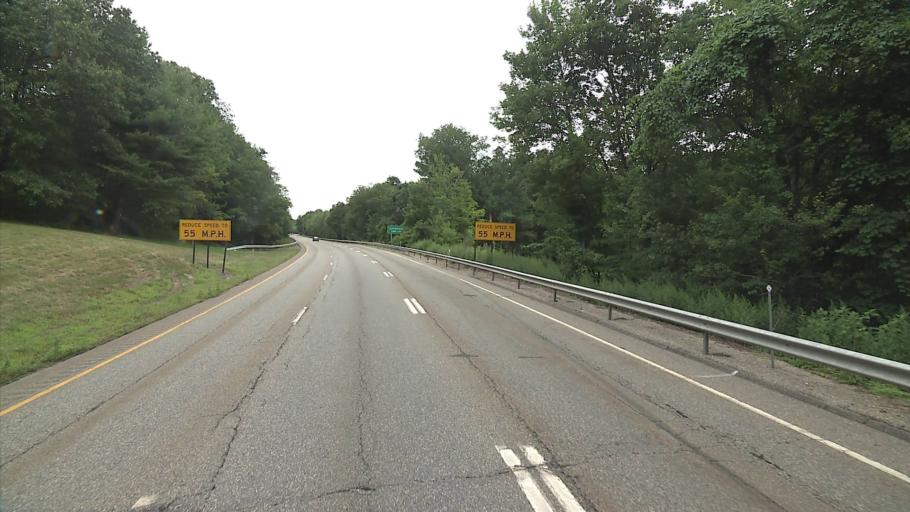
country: US
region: Connecticut
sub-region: Litchfield County
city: Thomaston
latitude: 41.7041
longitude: -73.0729
